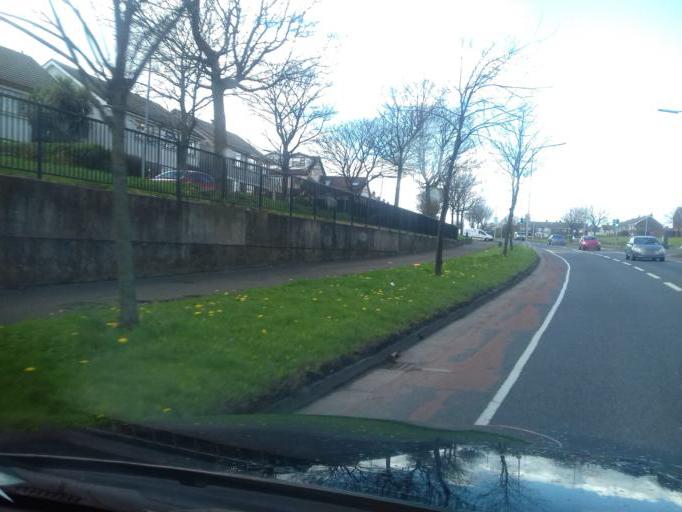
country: IE
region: Leinster
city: Donaghmede
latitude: 53.3906
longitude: -6.1590
